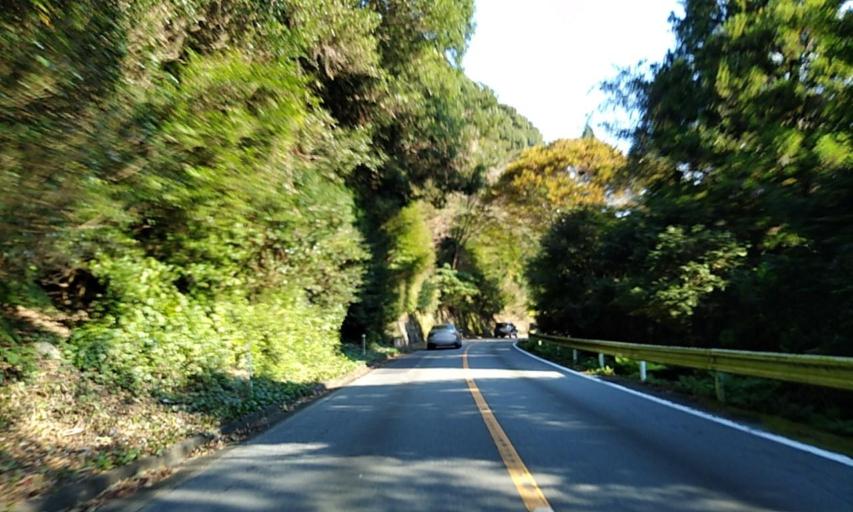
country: JP
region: Mie
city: Ise
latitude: 34.4430
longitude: 136.7524
